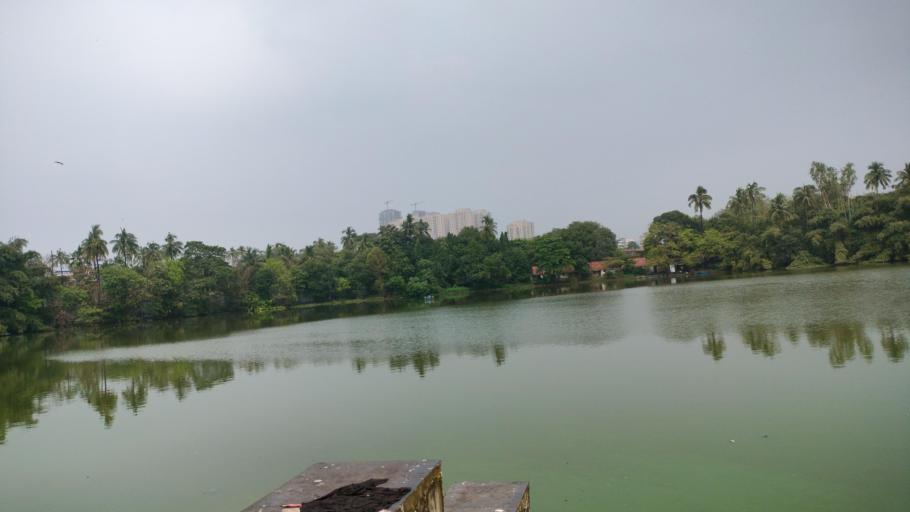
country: IN
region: Maharashtra
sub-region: Thane
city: Thane
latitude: 19.1991
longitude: 72.9799
